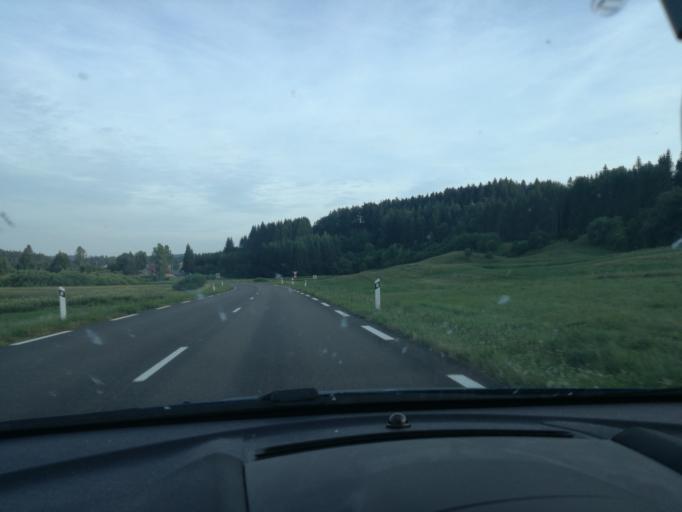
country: FR
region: Franche-Comte
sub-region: Departement du Jura
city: Morbier
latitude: 46.6129
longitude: 5.9596
